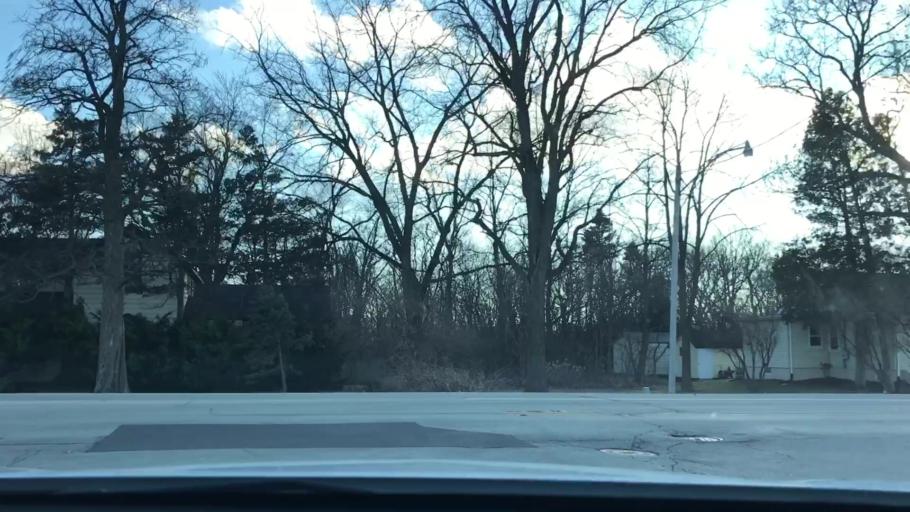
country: US
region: Illinois
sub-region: Kane County
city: Hampshire
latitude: 42.0885
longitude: -88.5251
